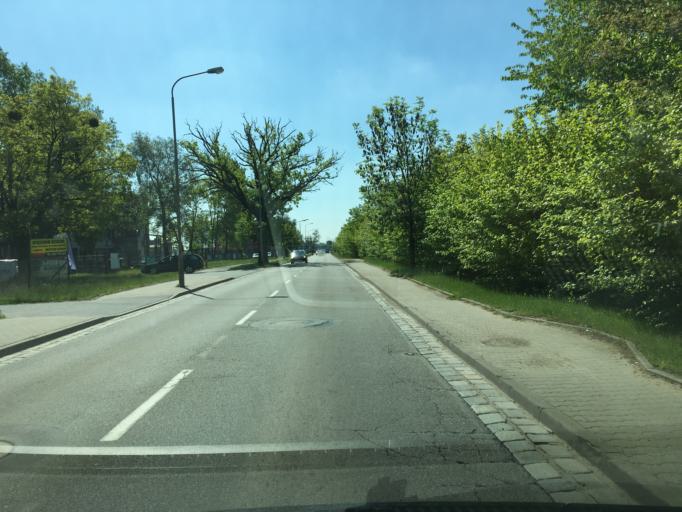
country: PL
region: Lower Silesian Voivodeship
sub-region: Powiat wroclawski
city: Bielany Wroclawskie
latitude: 51.0938
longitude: 16.9492
